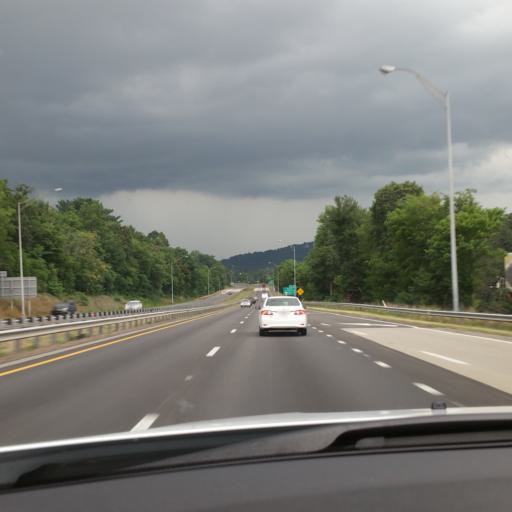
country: US
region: North Carolina
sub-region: Buncombe County
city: Woodfin
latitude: 35.6342
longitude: -82.5806
